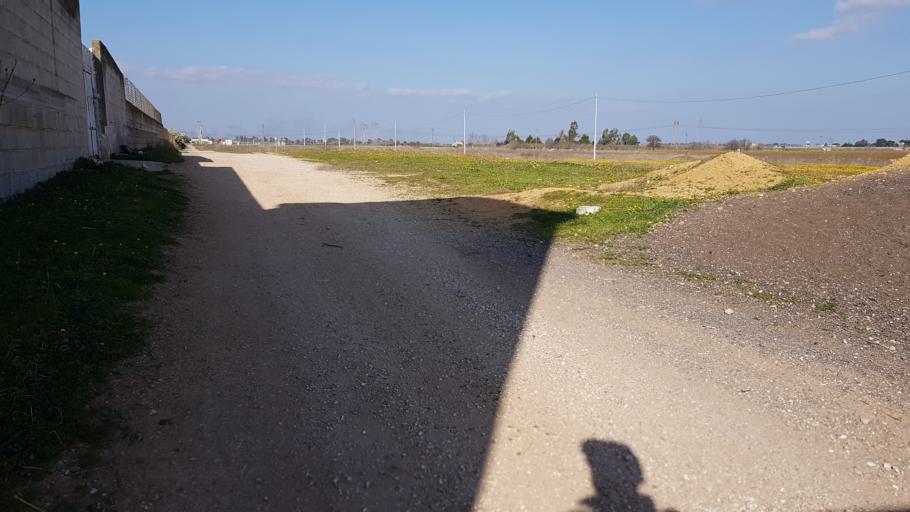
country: IT
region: Apulia
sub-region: Provincia di Brindisi
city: Brindisi
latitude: 40.5952
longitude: 17.8748
